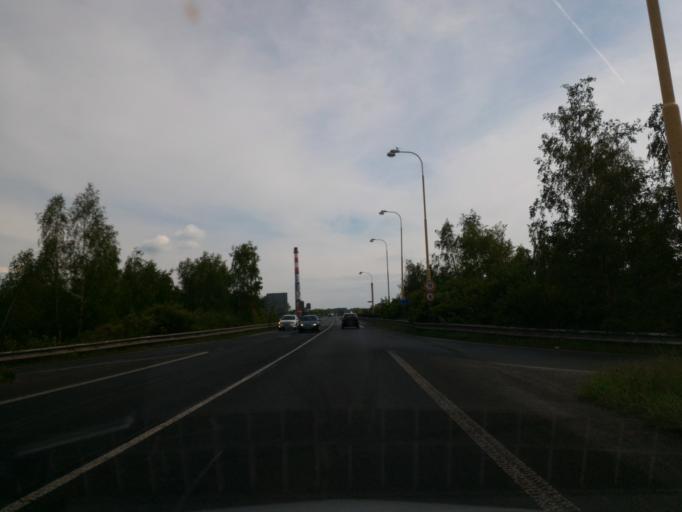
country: CZ
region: Liberecky
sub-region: Okres Ceska Lipa
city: Ceska Lipa
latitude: 50.6843
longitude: 14.5415
